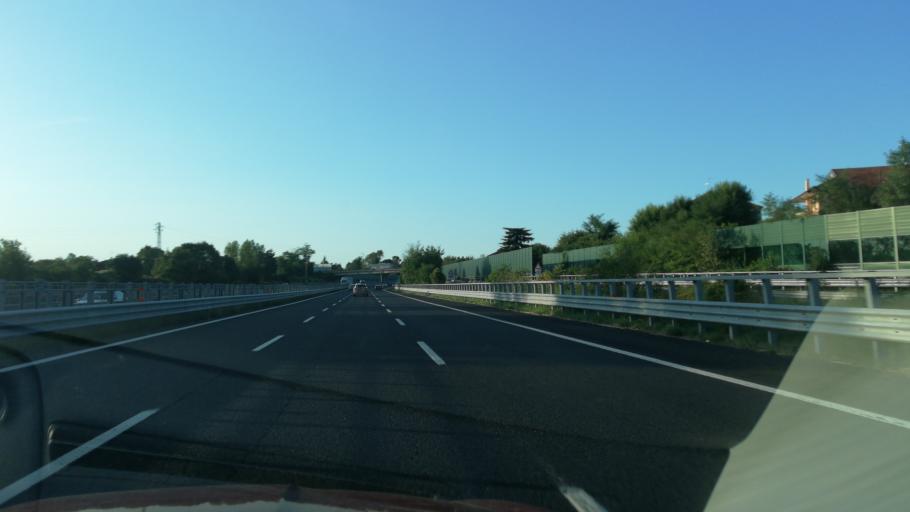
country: IT
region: Friuli Venezia Giulia
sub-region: Provincia di Udine
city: Passons
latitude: 46.0773
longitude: 13.1937
